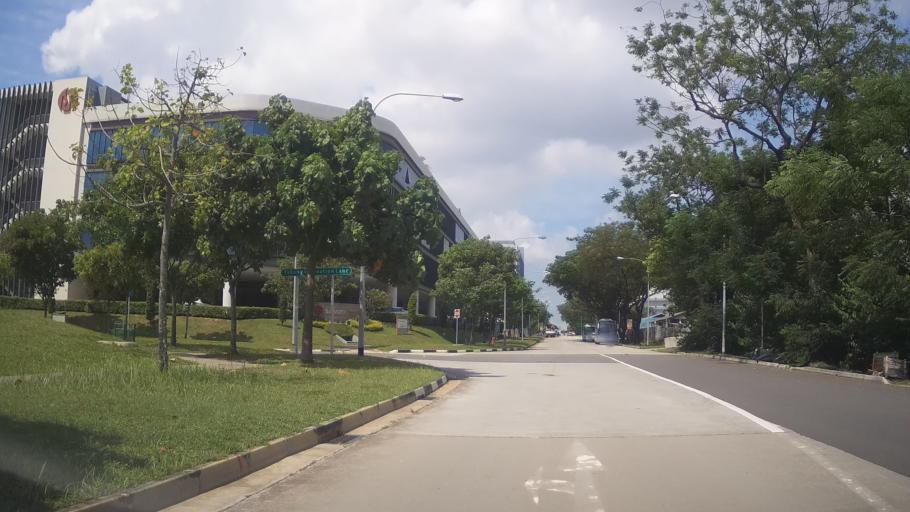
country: SG
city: Singapore
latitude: 1.3267
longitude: 103.7154
